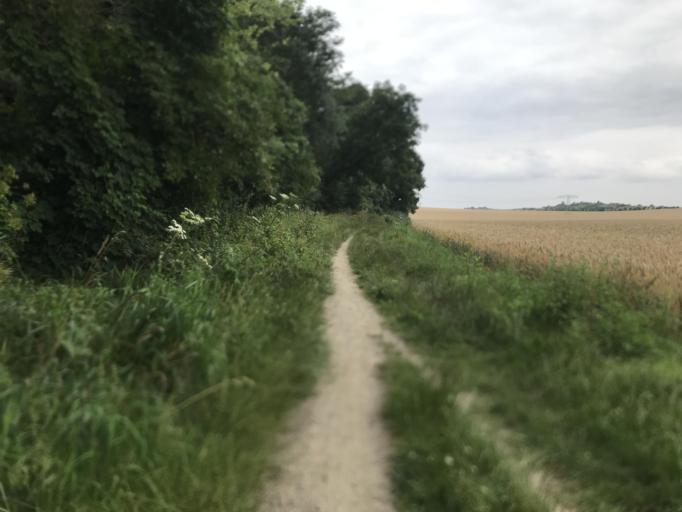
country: DE
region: Saxony-Anhalt
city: Neinstedt
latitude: 51.7555
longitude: 11.0749
